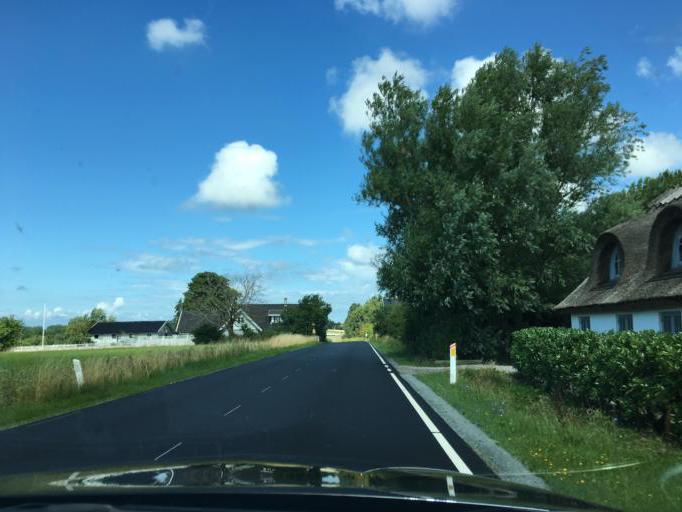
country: DK
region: Capital Region
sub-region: Gribskov Kommune
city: Helsinge
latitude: 56.0703
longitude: 12.1988
